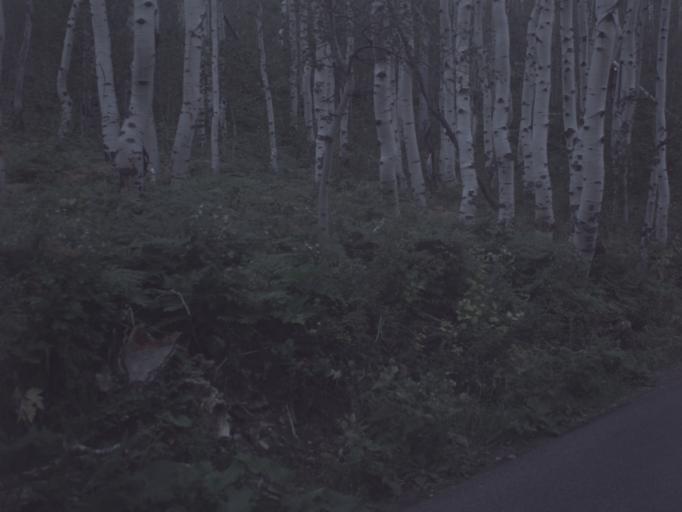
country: US
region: Utah
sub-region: Utah County
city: Lindon
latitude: 40.4187
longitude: -111.6069
